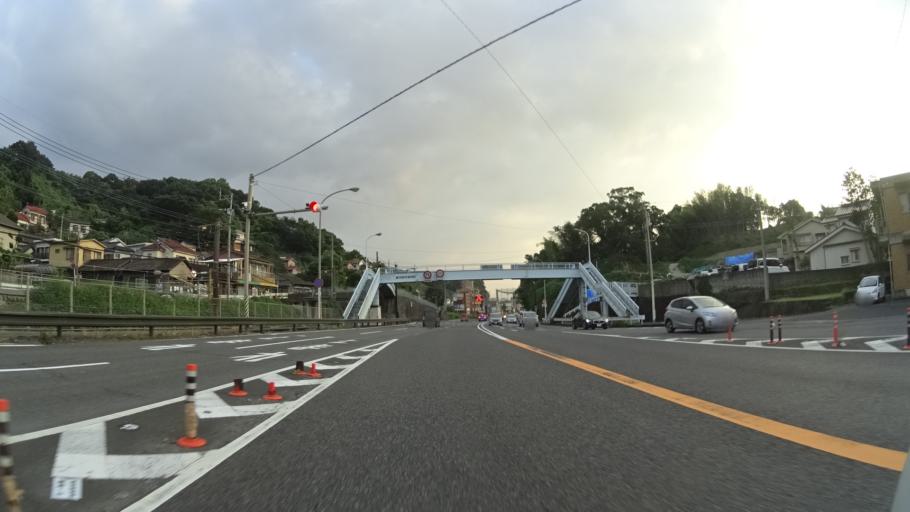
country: JP
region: Kagoshima
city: Kagoshima-shi
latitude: 31.6113
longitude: 130.5704
